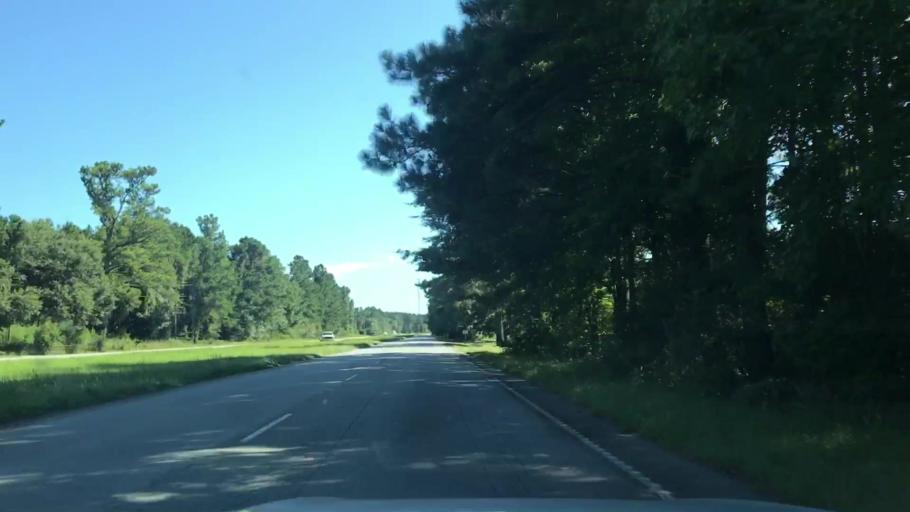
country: US
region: South Carolina
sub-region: Charleston County
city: Awendaw
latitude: 32.9992
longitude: -79.6443
